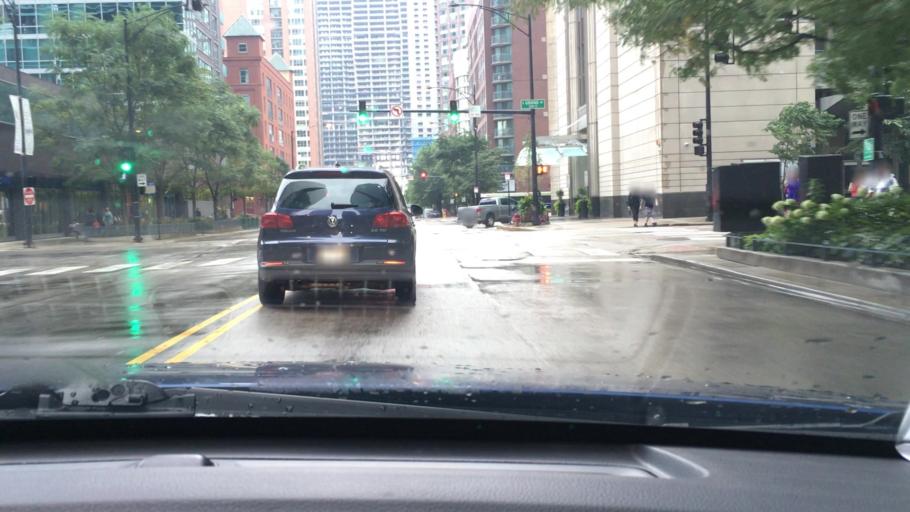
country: US
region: Illinois
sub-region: Cook County
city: Chicago
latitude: 41.8921
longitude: -87.6177
